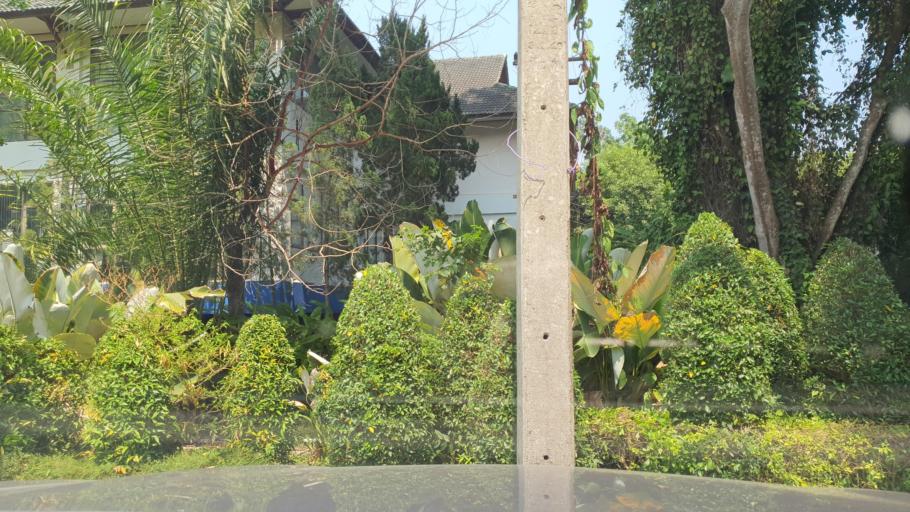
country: TH
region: Chiang Mai
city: Samoeng
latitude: 18.7878
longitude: 98.8418
